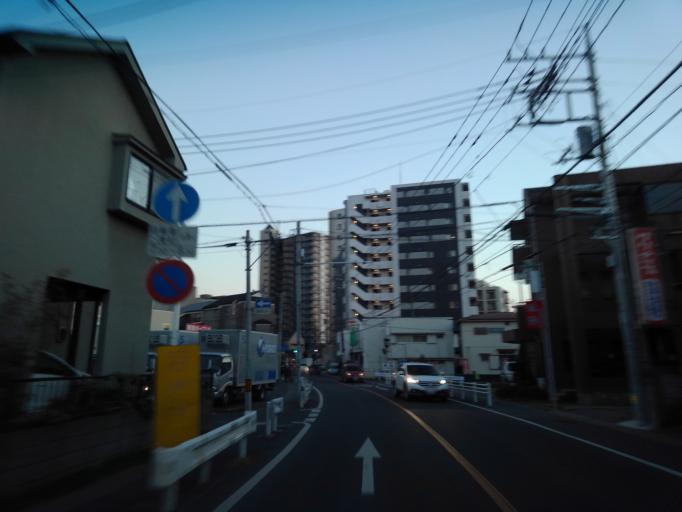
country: JP
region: Saitama
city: Tokorozawa
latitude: 35.7930
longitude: 139.4627
